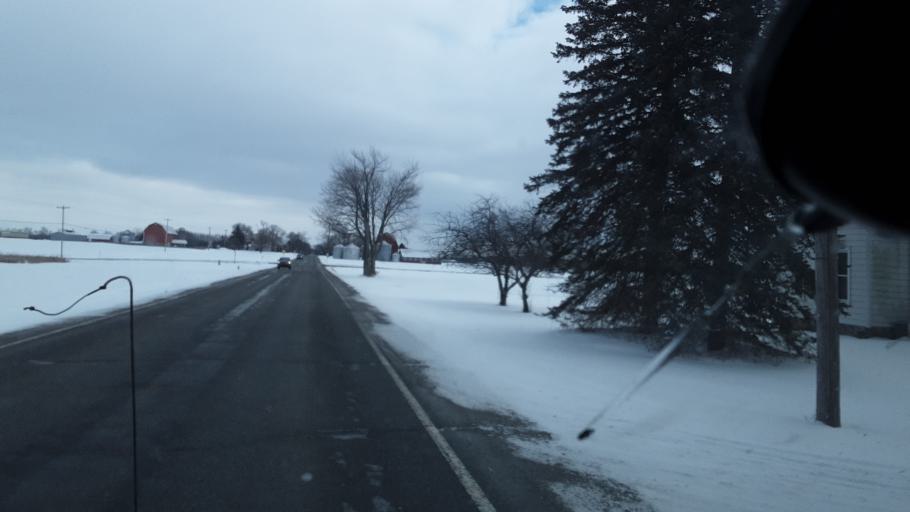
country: US
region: Michigan
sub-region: Ingham County
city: Holt
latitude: 42.5822
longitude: -84.5054
